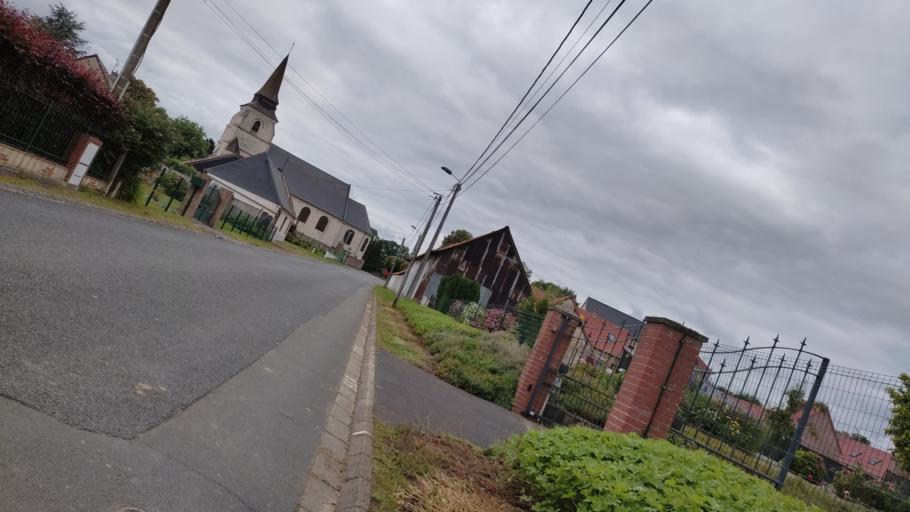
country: FR
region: Nord-Pas-de-Calais
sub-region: Departement du Pas-de-Calais
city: Beaumetz-les-Loges
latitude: 50.2559
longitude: 2.6456
